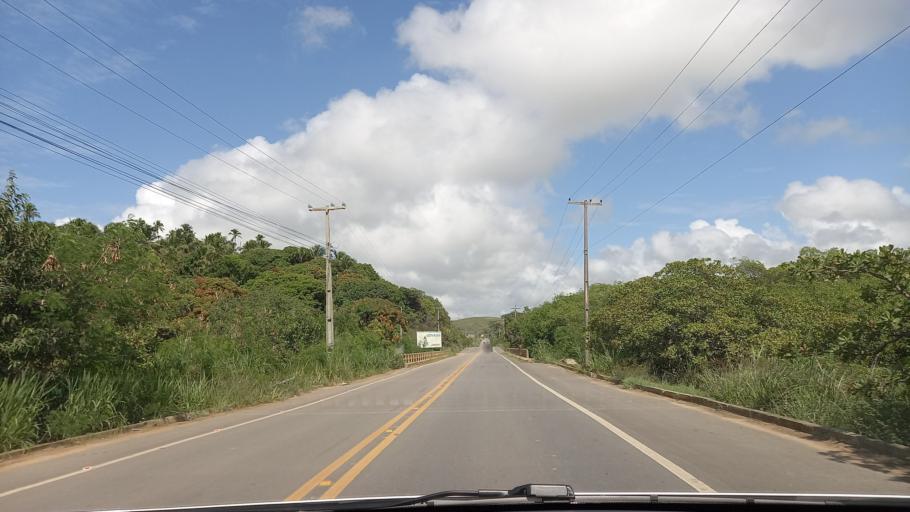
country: BR
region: Alagoas
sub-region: Maragogi
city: Maragogi
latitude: -8.9968
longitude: -35.2133
